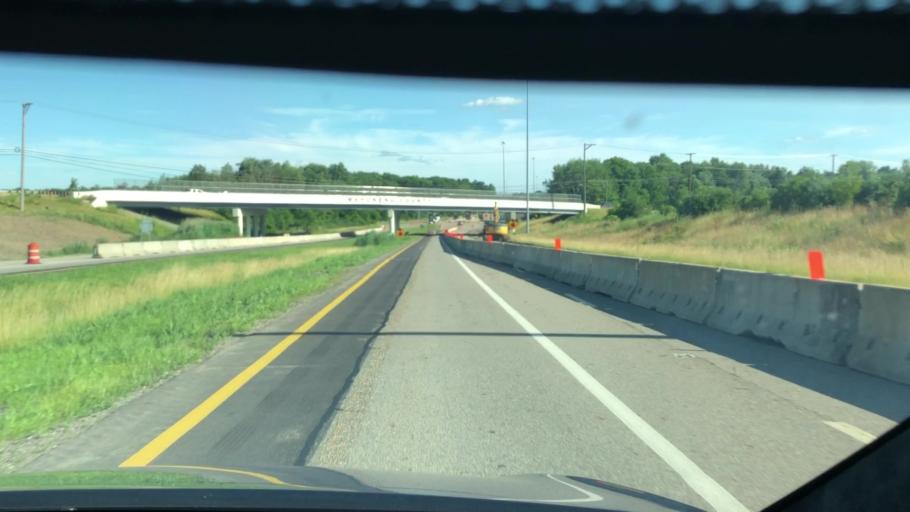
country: US
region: Ohio
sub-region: Mahoning County
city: Boardman
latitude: 40.9622
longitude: -80.6399
